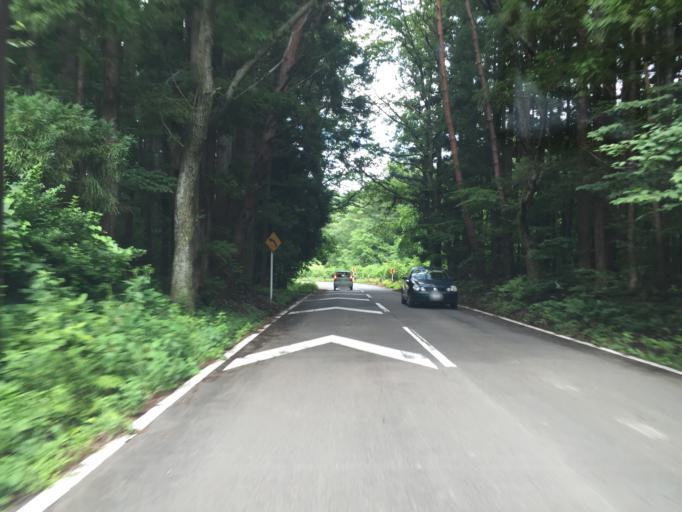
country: JP
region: Fukushima
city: Nihommatsu
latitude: 37.6813
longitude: 140.3324
